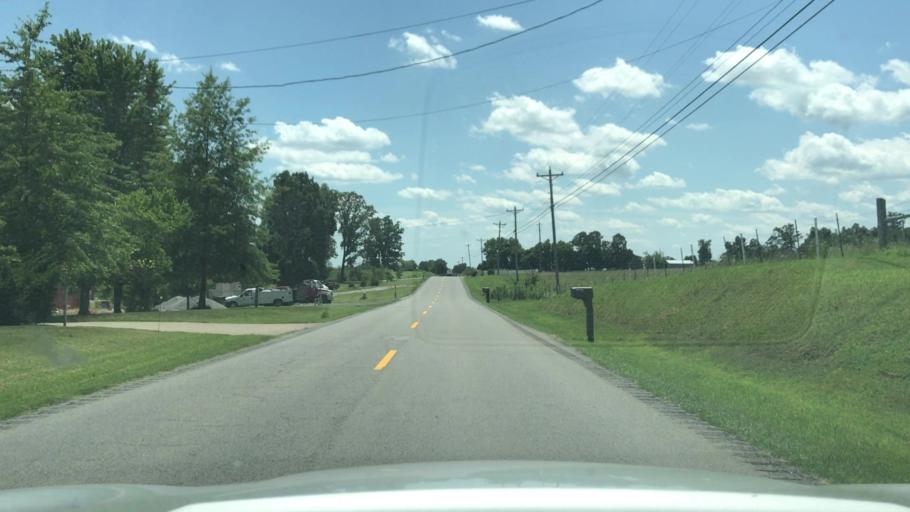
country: US
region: Kentucky
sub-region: Christian County
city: Hopkinsville
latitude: 36.9246
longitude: -87.4348
